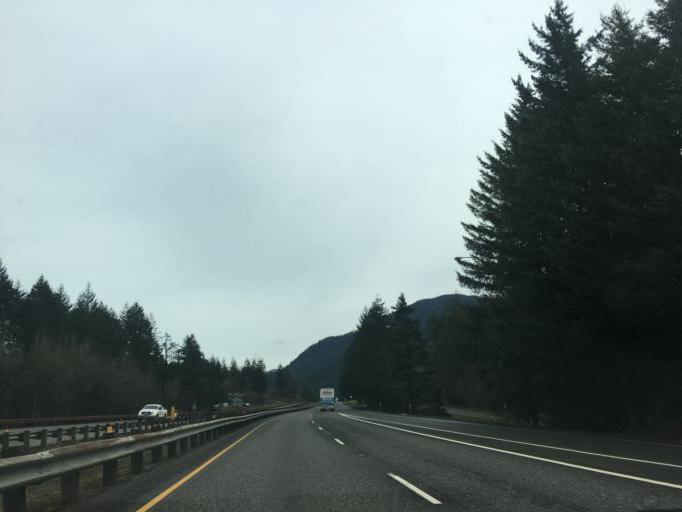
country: US
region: Oregon
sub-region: Hood River County
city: Cascade Locks
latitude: 45.6740
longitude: -121.8722
